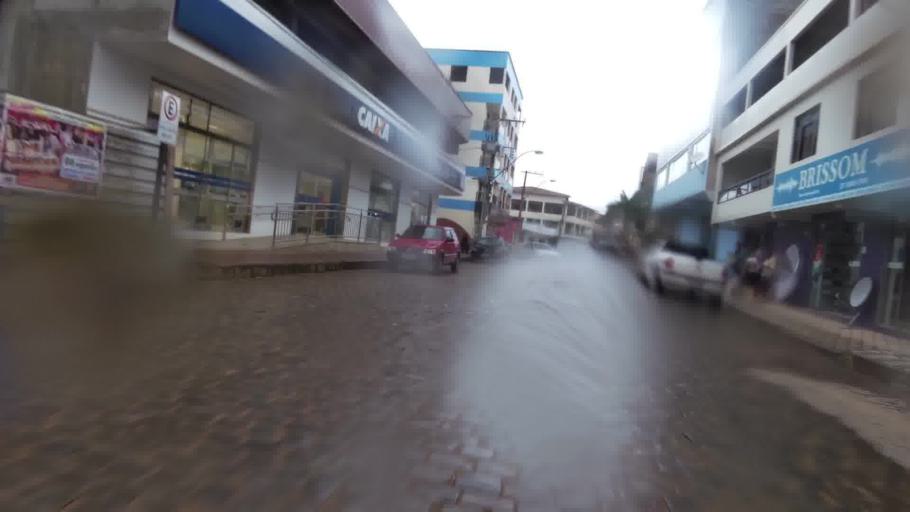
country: BR
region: Espirito Santo
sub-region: Alfredo Chaves
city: Alfredo Chaves
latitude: -20.6371
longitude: -40.7457
